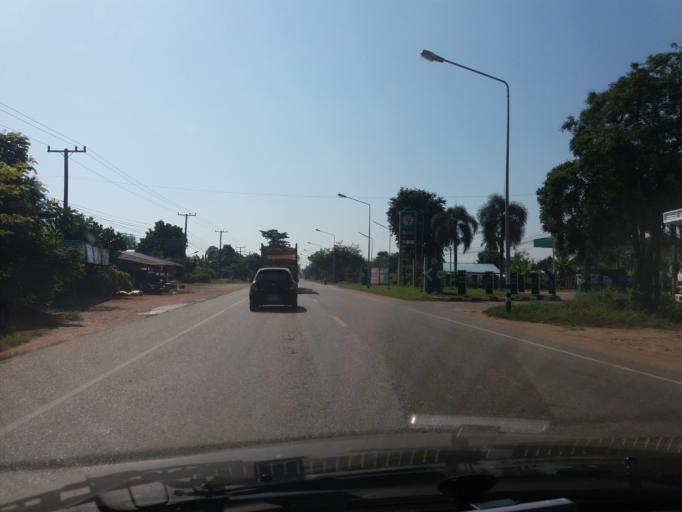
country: TH
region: Kamphaeng Phet
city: Khlong Khlung
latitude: 16.1679
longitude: 99.8003
